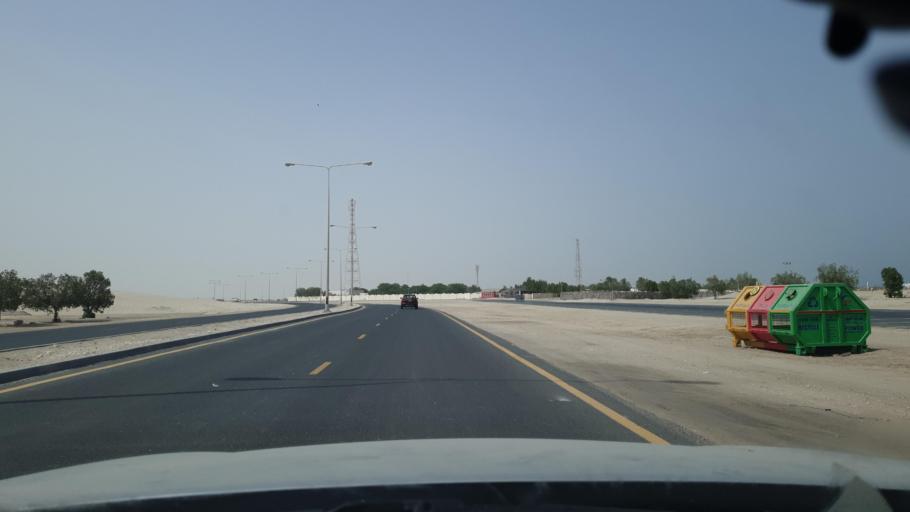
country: QA
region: Al Wakrah
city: Umm Sa'id
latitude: 24.8552
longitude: 51.5103
